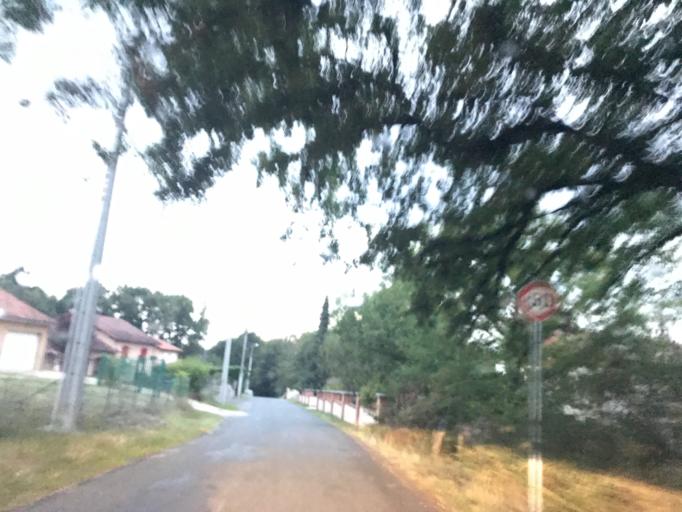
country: FR
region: Auvergne
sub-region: Departement du Puy-de-Dome
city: Peschadoires
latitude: 45.8363
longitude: 3.5227
